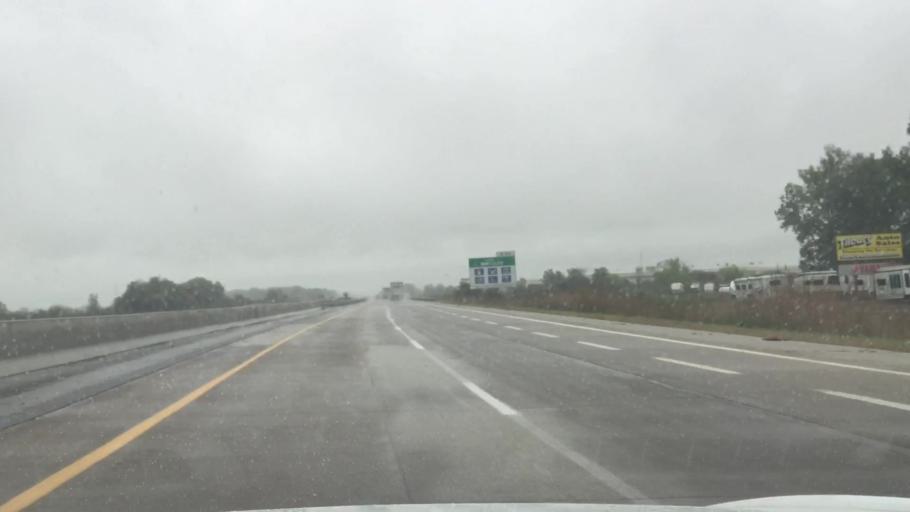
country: CA
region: Ontario
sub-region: Lambton County
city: Walpole Island
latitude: 42.2668
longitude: -82.4511
